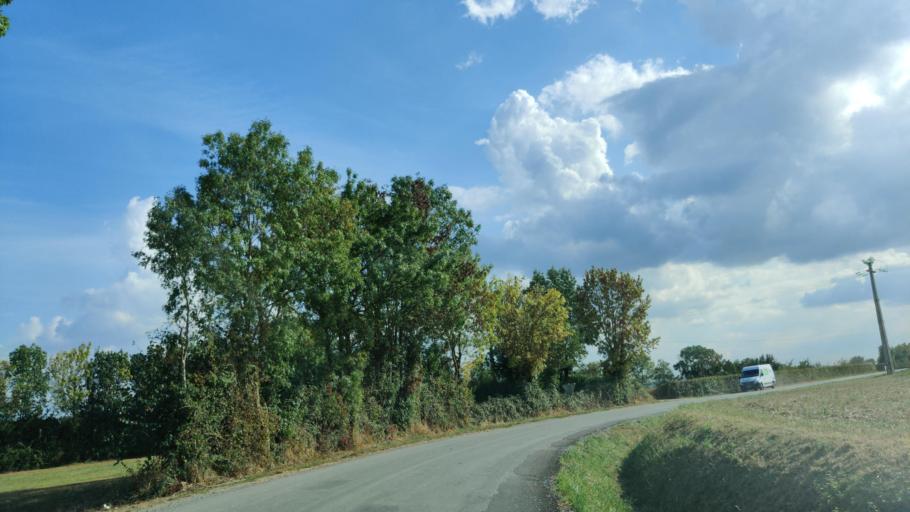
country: FR
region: Poitou-Charentes
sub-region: Departement des Deux-Sevres
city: Bessines
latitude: 46.2963
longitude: -0.5124
